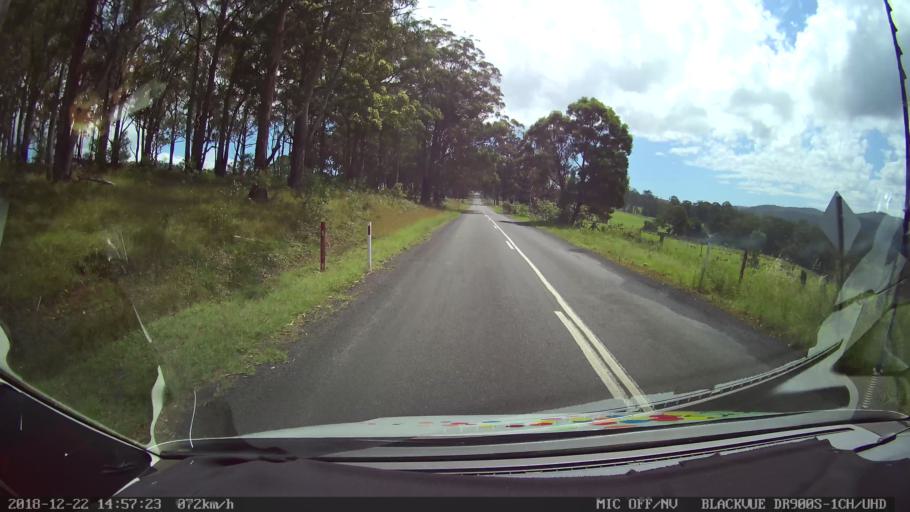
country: AU
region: New South Wales
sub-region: Bellingen
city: Dorrigo
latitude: -30.2340
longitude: 152.5018
